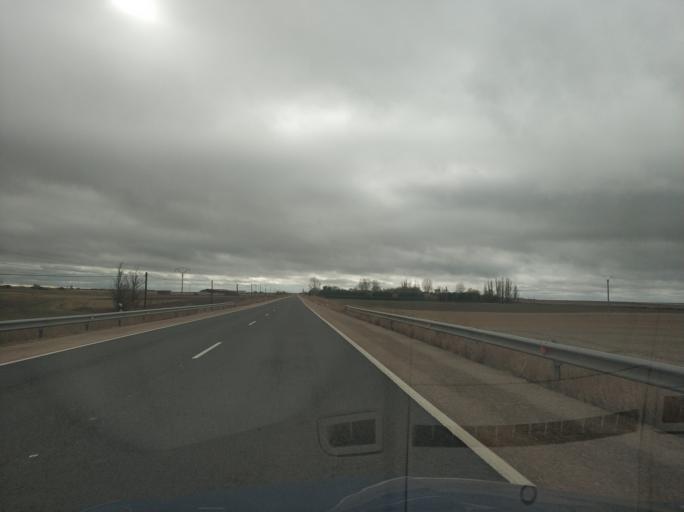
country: ES
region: Castille and Leon
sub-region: Provincia de Salamanca
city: Pedrosillo el Ralo
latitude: 41.0542
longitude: -5.5544
